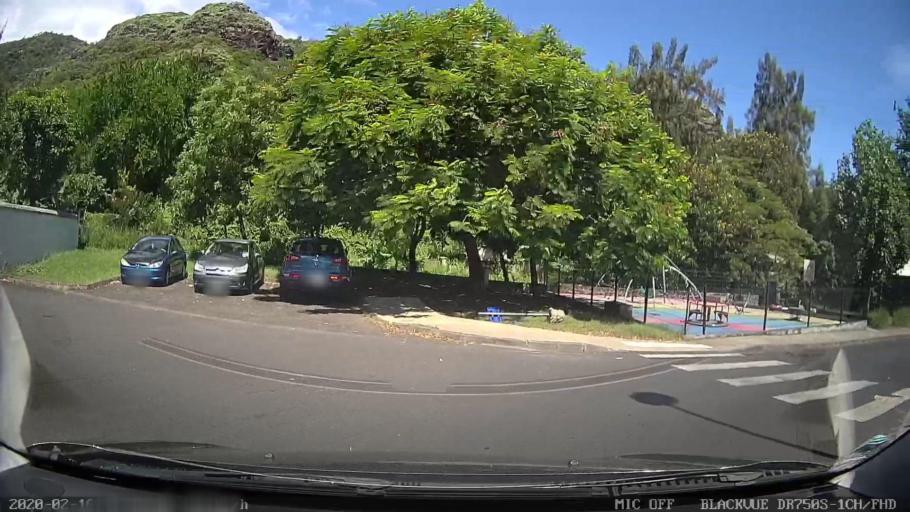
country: RE
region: Reunion
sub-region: Reunion
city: Saint-Denis
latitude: -20.8813
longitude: 55.4400
